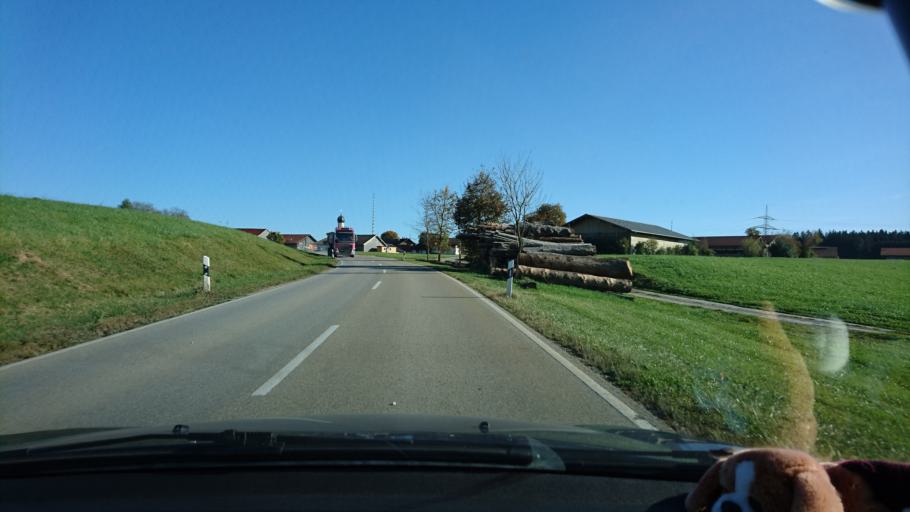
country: DE
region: Bavaria
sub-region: Upper Bavaria
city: Zorneding
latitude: 48.0619
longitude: 11.8478
